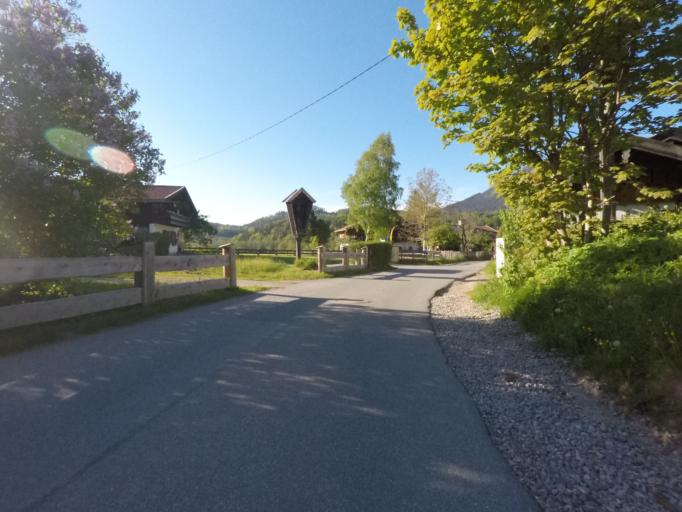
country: DE
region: Bavaria
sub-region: Upper Bavaria
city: Fischbachau
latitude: 47.6886
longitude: 11.9609
